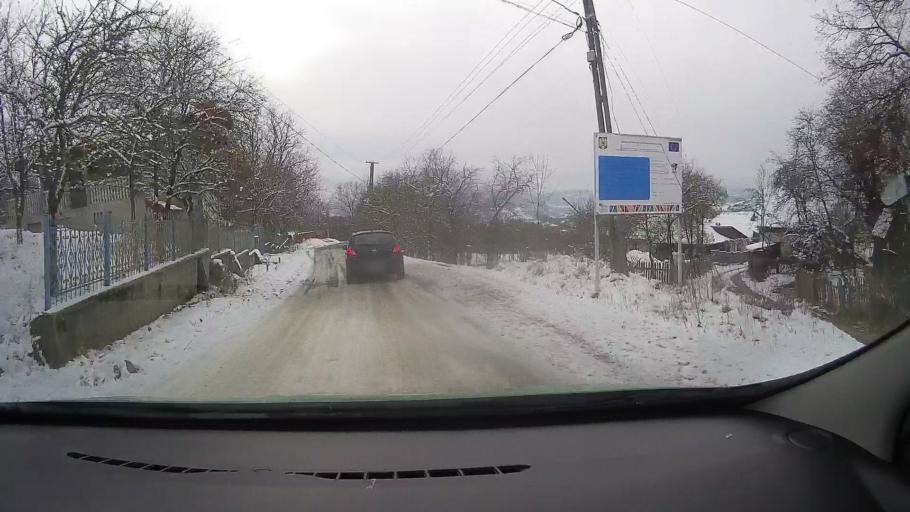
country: RO
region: Alba
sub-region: Comuna Almasu Mare
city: Almasu Mare
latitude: 46.0880
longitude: 23.1293
